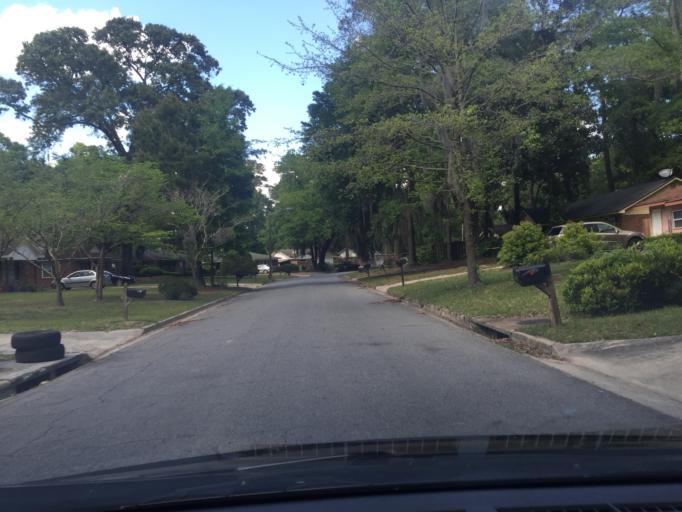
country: US
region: Georgia
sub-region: Chatham County
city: Montgomery
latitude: 31.9906
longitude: -81.1212
